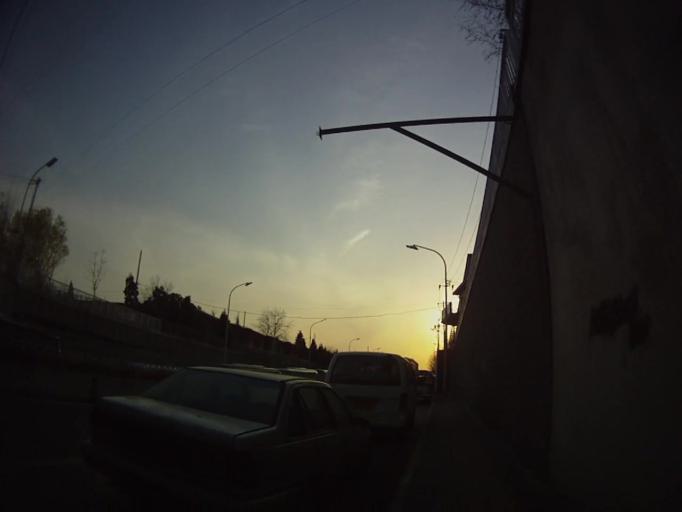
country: CN
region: Beijing
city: Longtan
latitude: 39.8799
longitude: 116.4261
